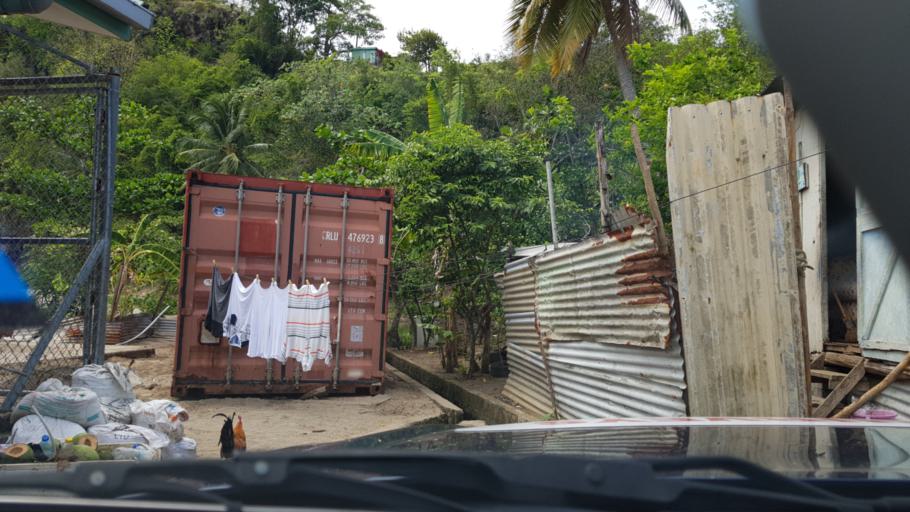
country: LC
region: Anse-la-Raye
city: Anse La Raye
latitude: 13.9416
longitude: -61.0433
